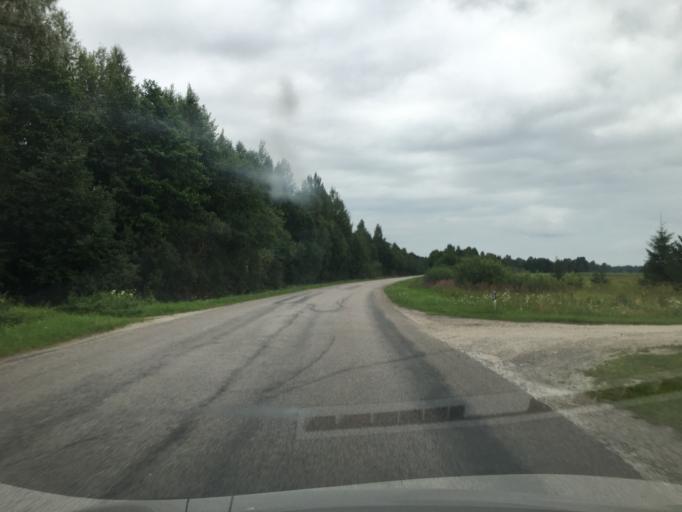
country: EE
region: Raplamaa
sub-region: Jaervakandi vald
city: Jarvakandi
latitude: 58.8044
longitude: 24.9201
